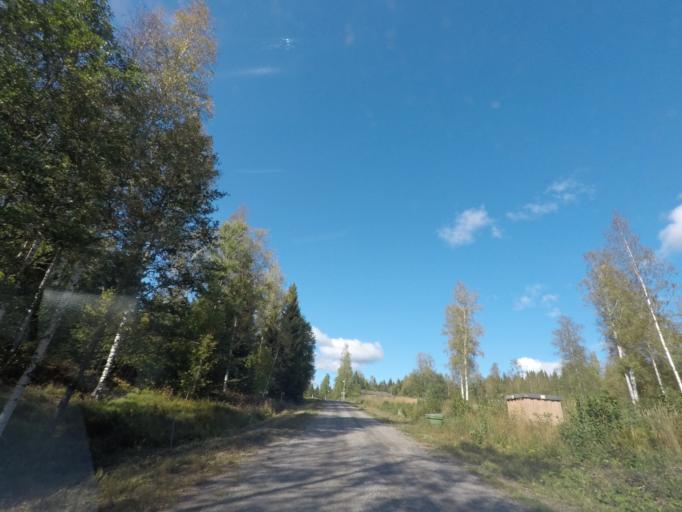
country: SE
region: Vaestmanland
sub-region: Skinnskattebergs Kommun
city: Skinnskatteberg
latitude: 59.8286
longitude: 15.5216
